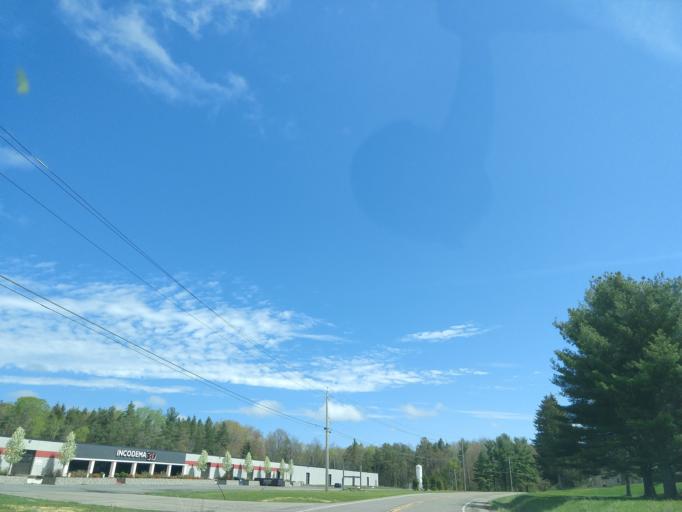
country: US
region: New York
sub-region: Tompkins County
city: Dryden
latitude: 42.4969
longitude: -76.3707
